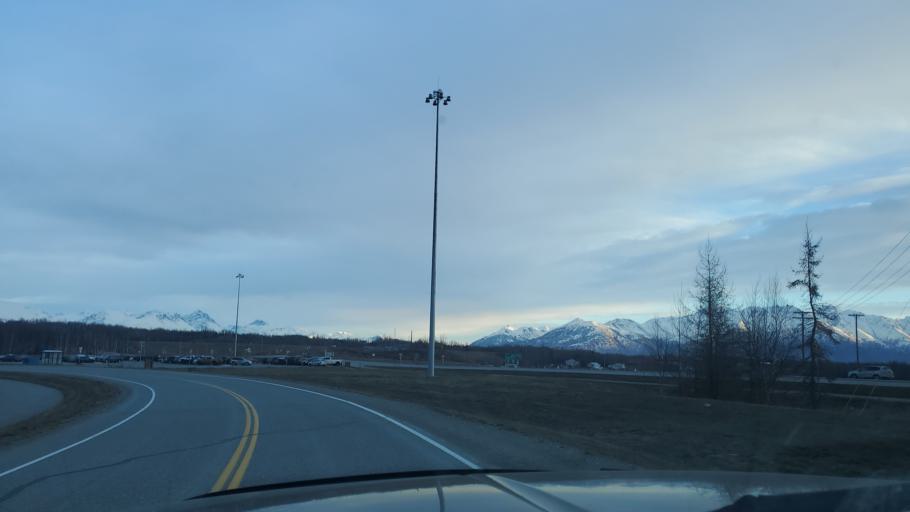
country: US
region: Alaska
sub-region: Matanuska-Susitna Borough
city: Gateway
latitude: 61.5639
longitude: -149.2662
